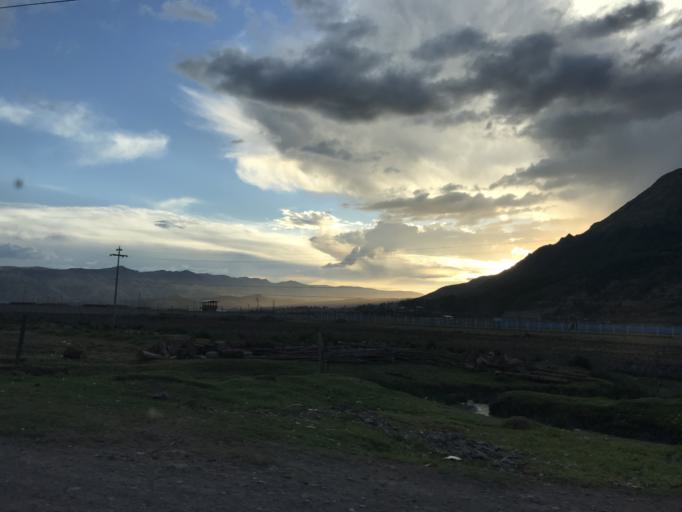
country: PE
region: Cusco
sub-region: Provincia de Anta
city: Huarocondo
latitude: -13.4244
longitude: -72.2043
